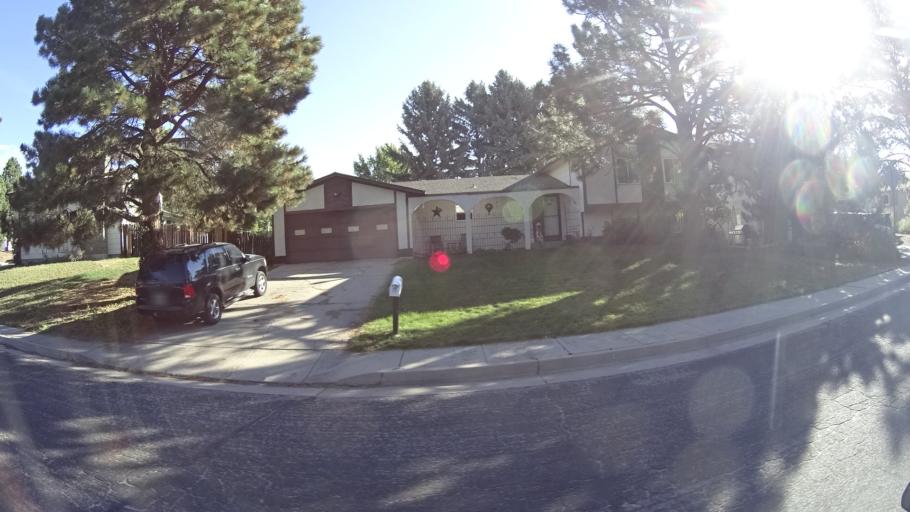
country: US
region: Colorado
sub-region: El Paso County
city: Cimarron Hills
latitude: 38.9097
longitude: -104.7541
